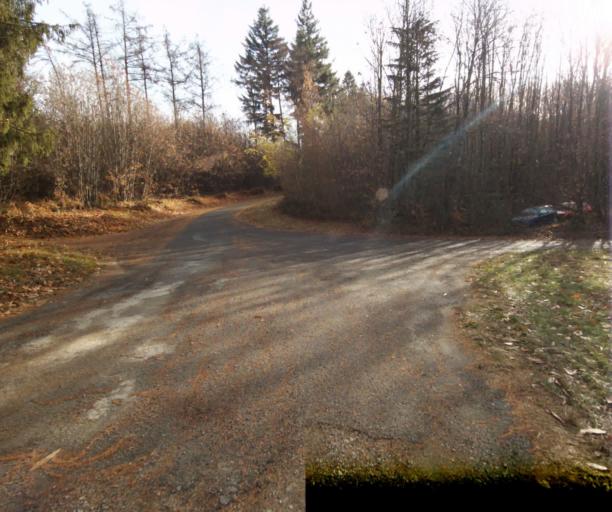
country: FR
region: Limousin
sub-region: Departement de la Correze
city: Sainte-Fortunade
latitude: 45.1934
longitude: 1.7535
